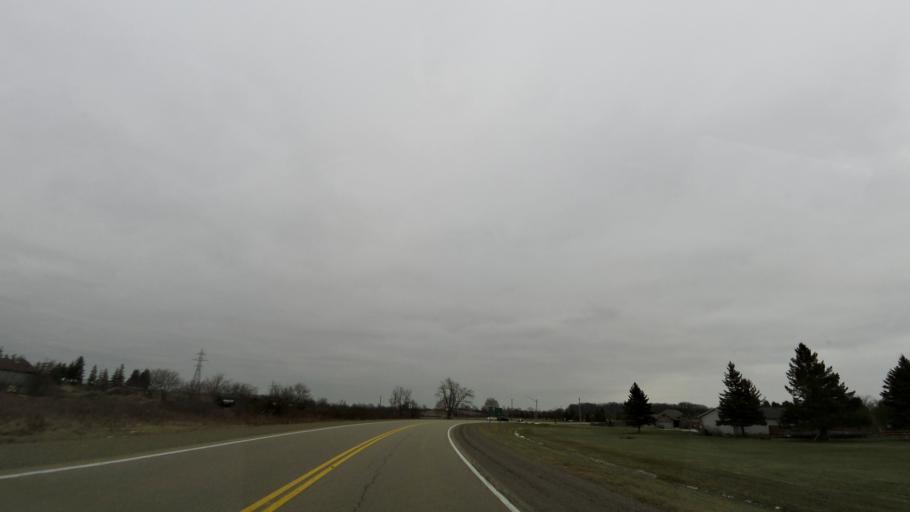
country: CA
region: Ontario
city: Brantford
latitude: 43.1194
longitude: -80.1197
